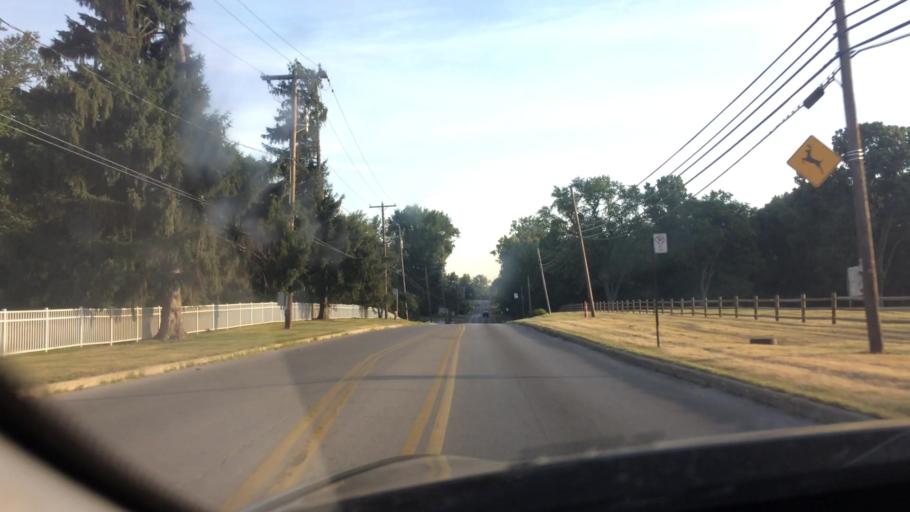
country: US
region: Ohio
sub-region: Lucas County
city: Ottawa Hills
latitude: 41.6536
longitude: -83.6410
